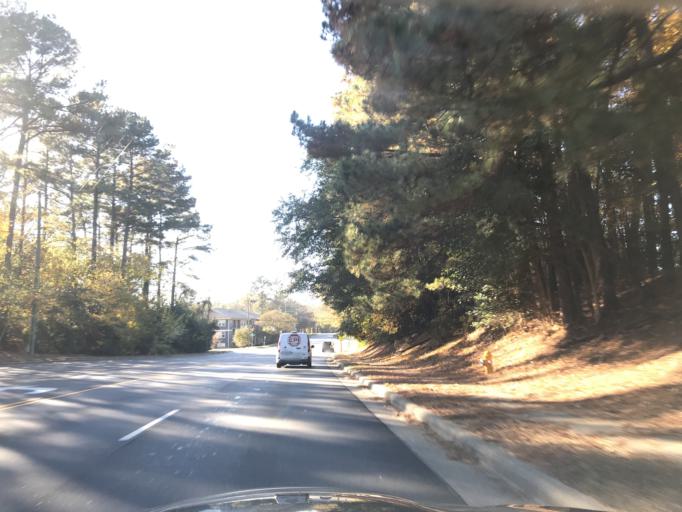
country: US
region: North Carolina
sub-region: Wake County
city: Raleigh
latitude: 35.7678
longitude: -78.6214
